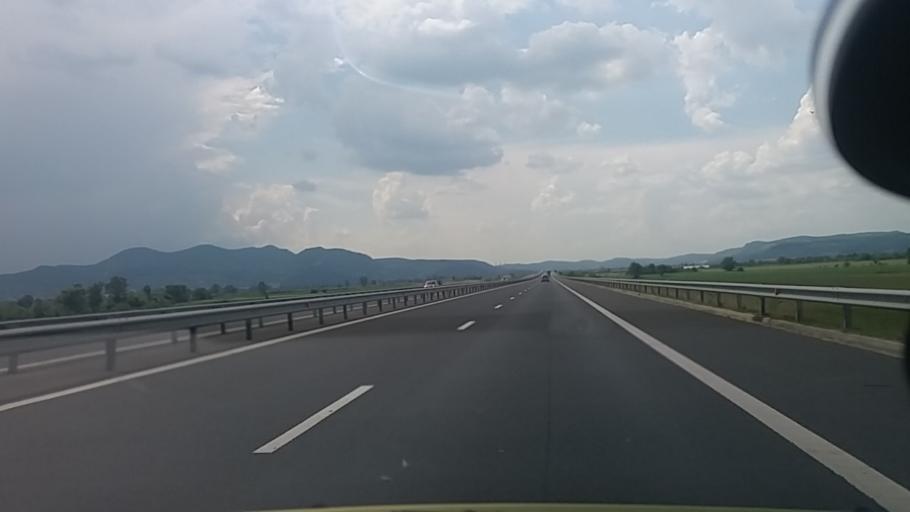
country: RO
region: Hunedoara
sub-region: Comuna Harau
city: Harau
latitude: 45.8893
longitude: 22.9687
